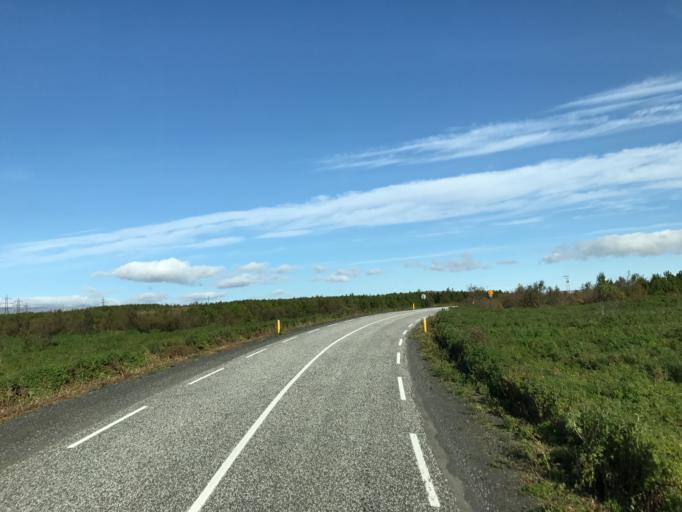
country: IS
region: Capital Region
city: Mosfellsbaer
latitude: 64.0939
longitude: -21.7104
